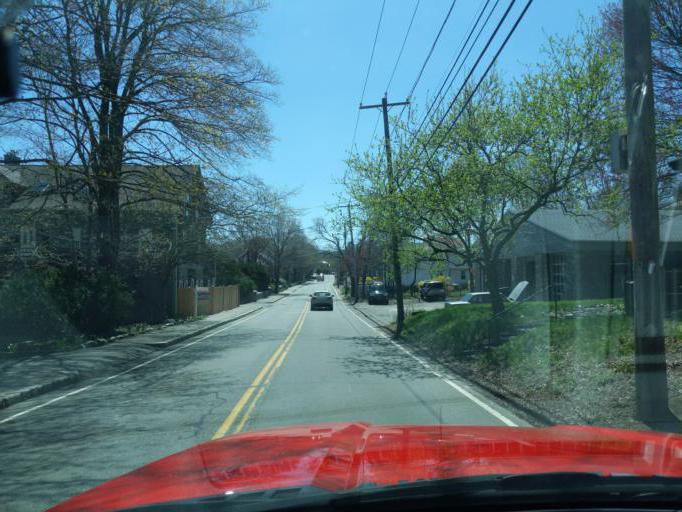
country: US
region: Massachusetts
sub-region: Essex County
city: Rockport
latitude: 42.6701
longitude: -70.6242
